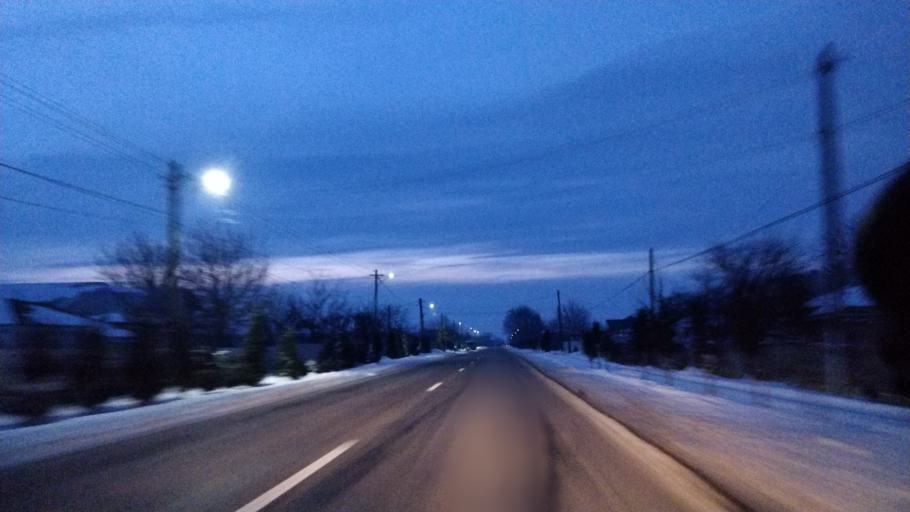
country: RO
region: Vrancea
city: Vulturu de Sus
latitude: 45.6359
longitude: 27.3781
